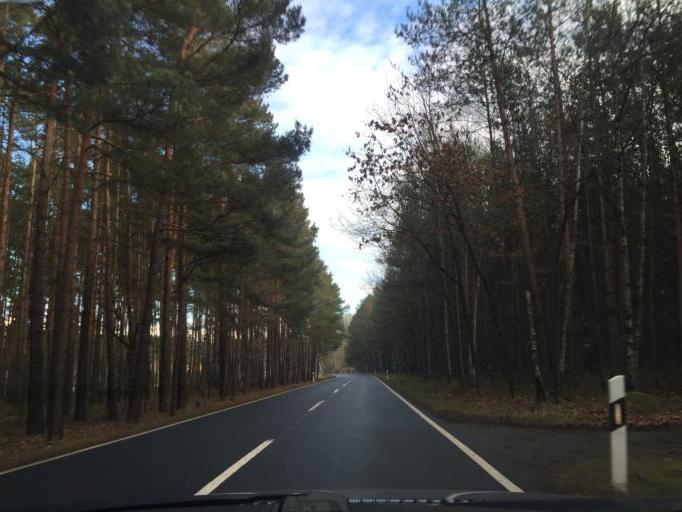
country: DE
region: Saxony
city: Tauscha
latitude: 51.2444
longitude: 13.7656
